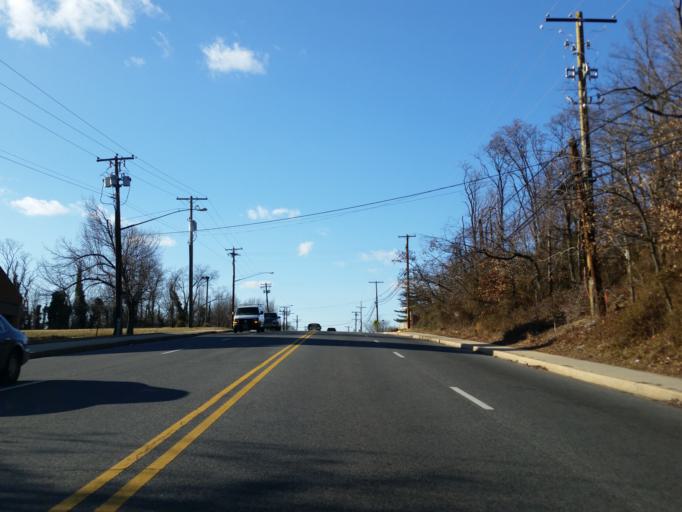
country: US
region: Maryland
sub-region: Prince George's County
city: Chillum
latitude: 38.9572
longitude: -76.9846
